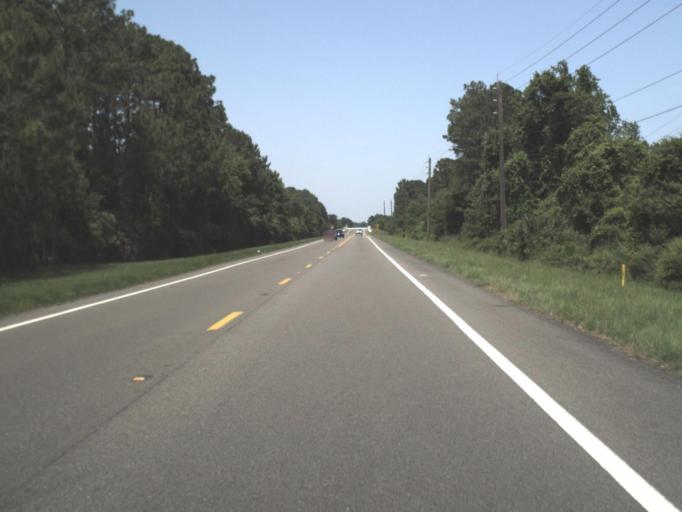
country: US
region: Florida
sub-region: Nassau County
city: Yulee
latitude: 30.5703
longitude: -81.6121
